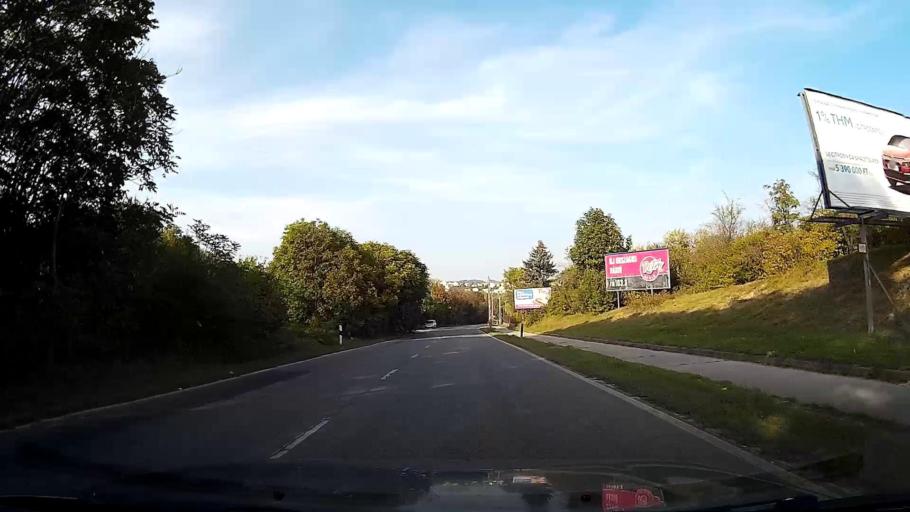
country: HU
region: Pest
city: Budaors
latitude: 47.4536
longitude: 18.9917
